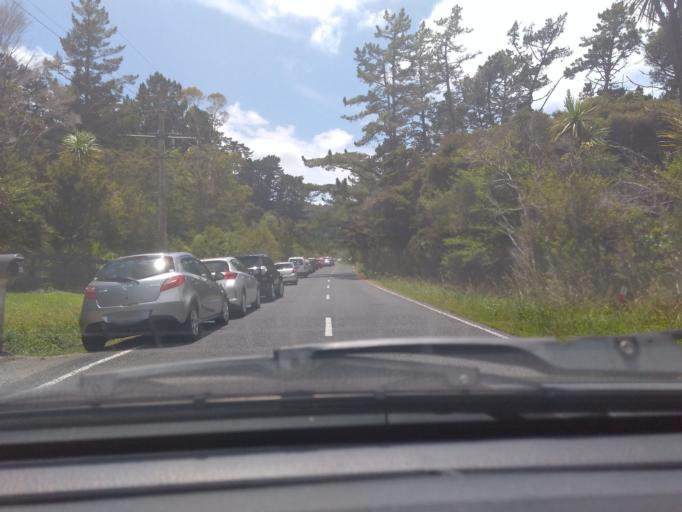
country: NZ
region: Auckland
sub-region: Auckland
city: Rothesay Bay
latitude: -36.6760
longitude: 174.7041
